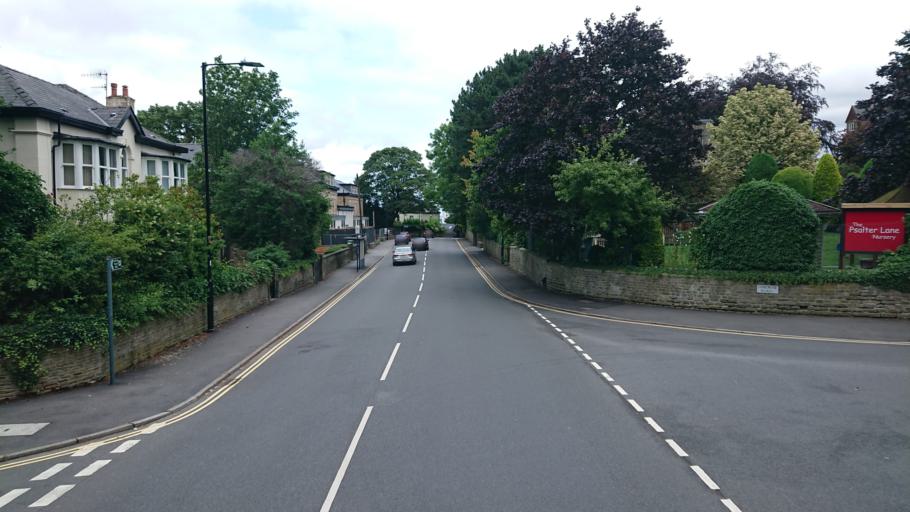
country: GB
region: England
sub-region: Sheffield
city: Sheffield
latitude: 53.3642
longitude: -1.5023
